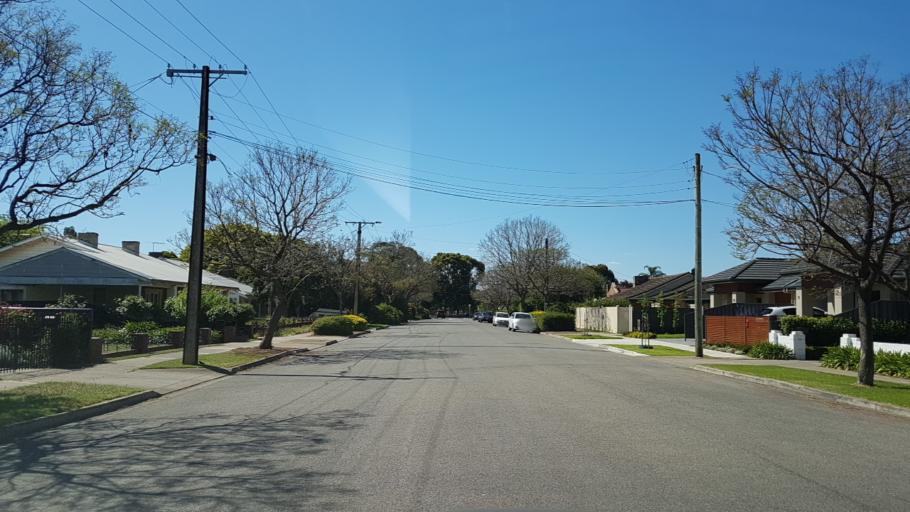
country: AU
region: South Australia
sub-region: Marion
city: South Plympton
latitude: -34.9660
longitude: 138.5606
